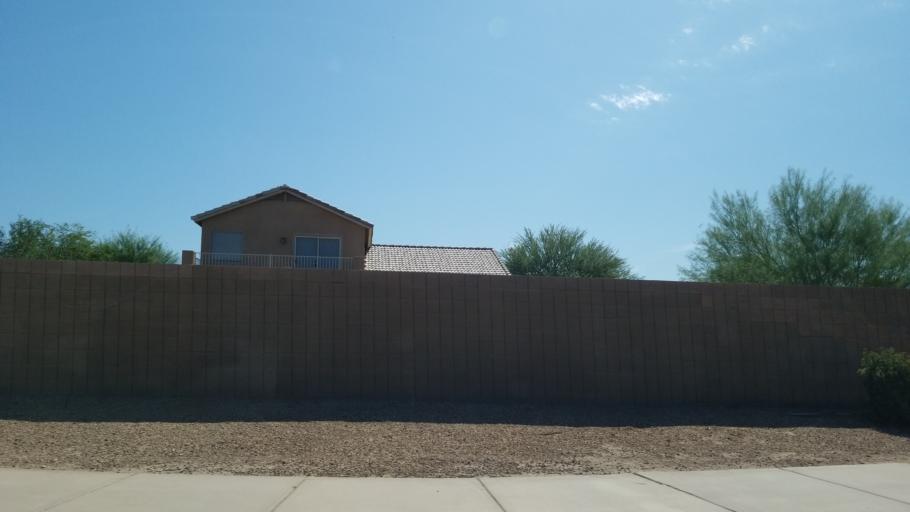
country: US
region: Arizona
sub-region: Maricopa County
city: Tolleson
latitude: 33.4125
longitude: -112.2213
